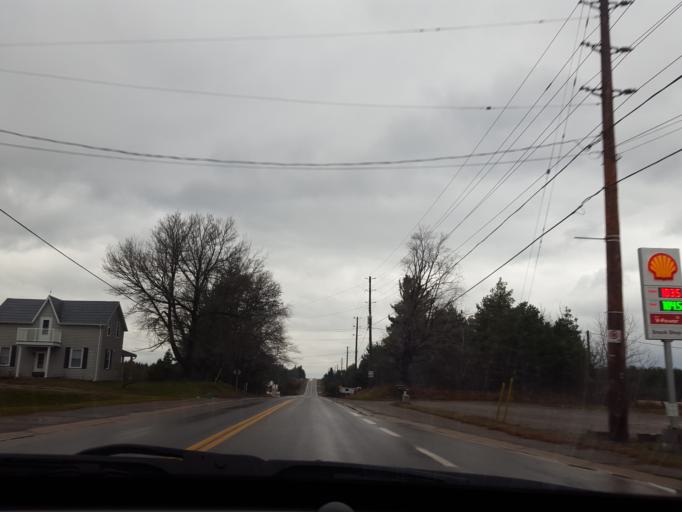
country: CA
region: Ontario
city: Uxbridge
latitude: 44.0460
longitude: -79.1475
